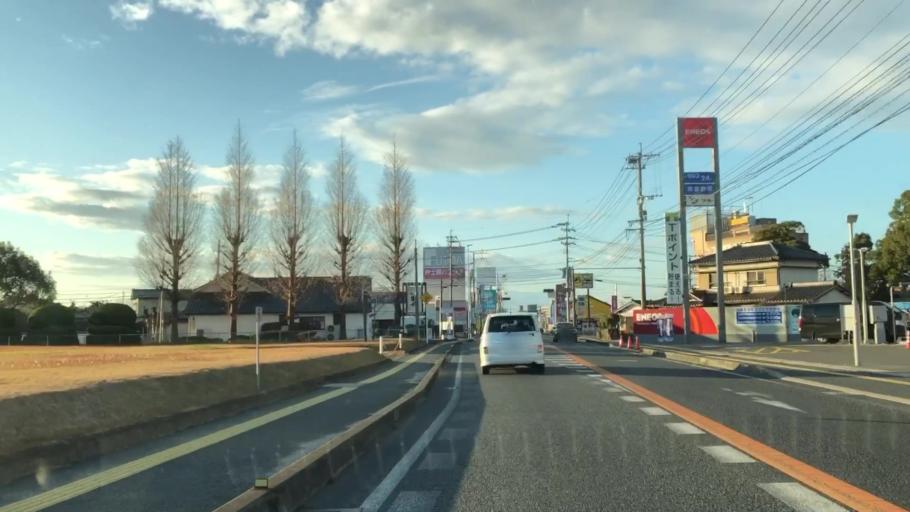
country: JP
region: Oita
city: Bungo-Takada-shi
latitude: 33.5283
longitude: 131.3394
